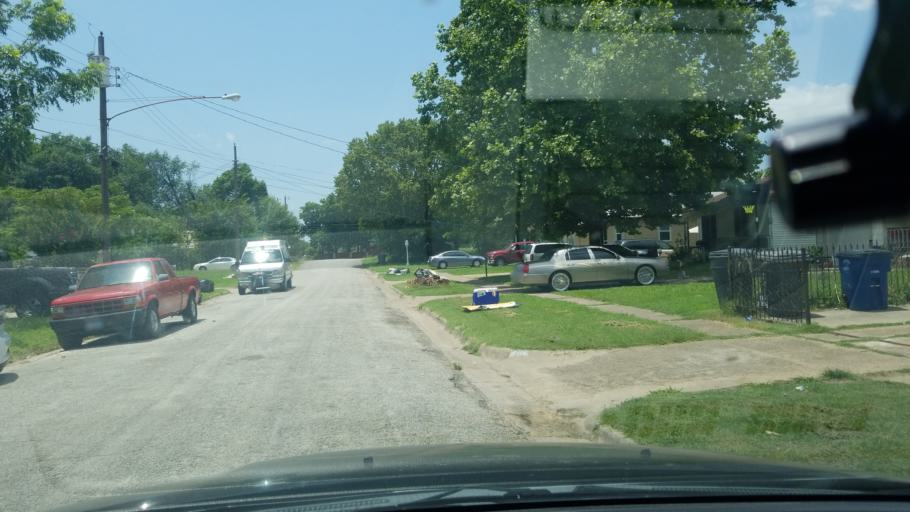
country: US
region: Texas
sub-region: Dallas County
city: Balch Springs
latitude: 32.7294
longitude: -96.6643
